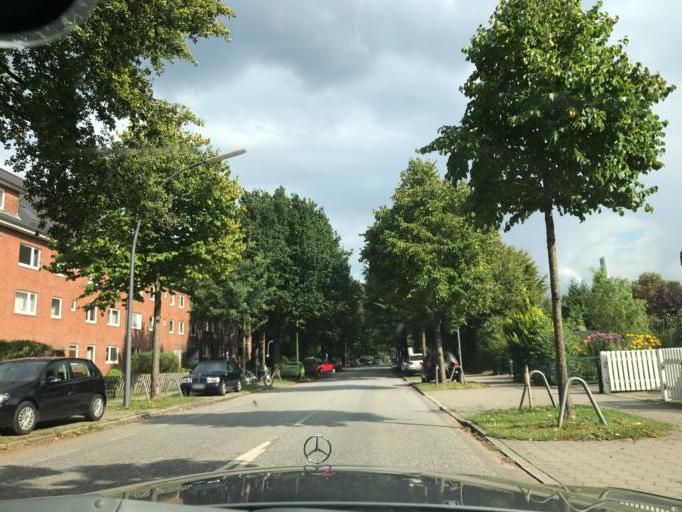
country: DE
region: Hamburg
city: Stellingen
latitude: 53.5990
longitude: 9.9420
